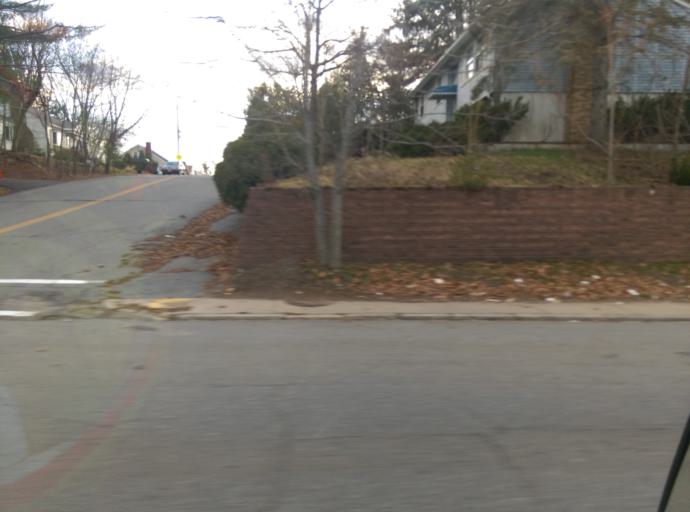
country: US
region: Massachusetts
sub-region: Essex County
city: Lawrence
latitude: 42.6869
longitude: -71.1571
